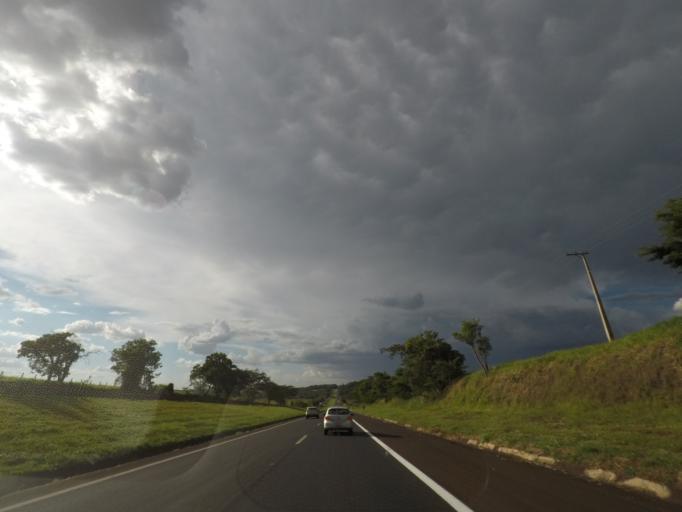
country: BR
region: Sao Paulo
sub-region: Jardinopolis
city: Jardinopolis
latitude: -21.0739
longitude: -47.8085
